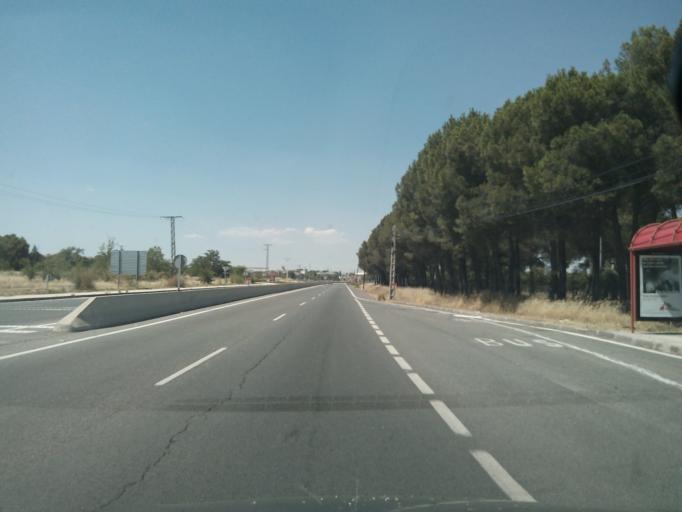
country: ES
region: Madrid
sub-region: Provincia de Madrid
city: Torrejon de Ardoz
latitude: 40.4877
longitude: -3.4780
